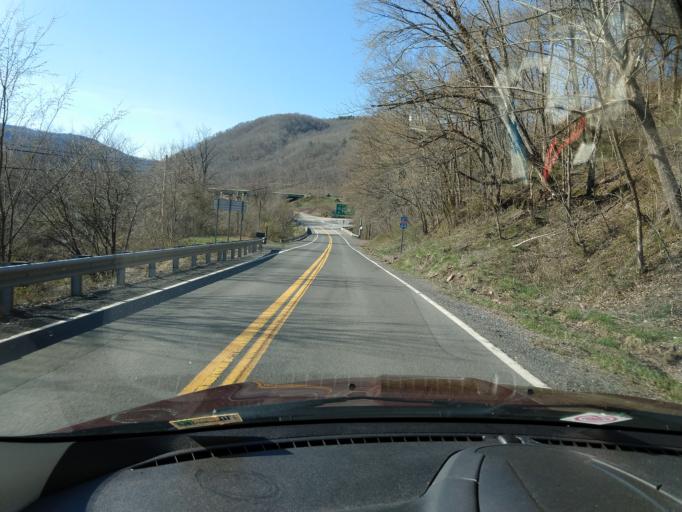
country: US
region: West Virginia
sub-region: Summers County
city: Hinton
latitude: 37.7774
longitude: -80.8909
